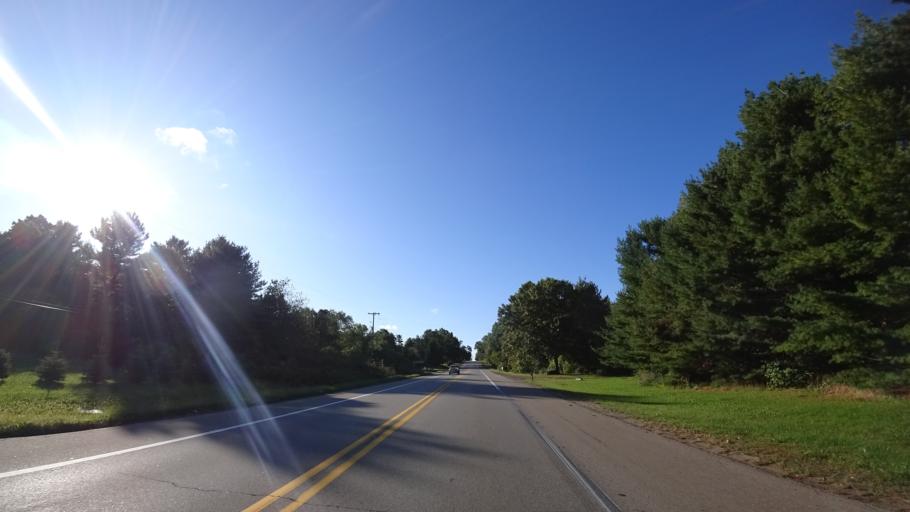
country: US
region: Michigan
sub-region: Kent County
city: Grandville
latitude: 42.9340
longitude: -85.7743
